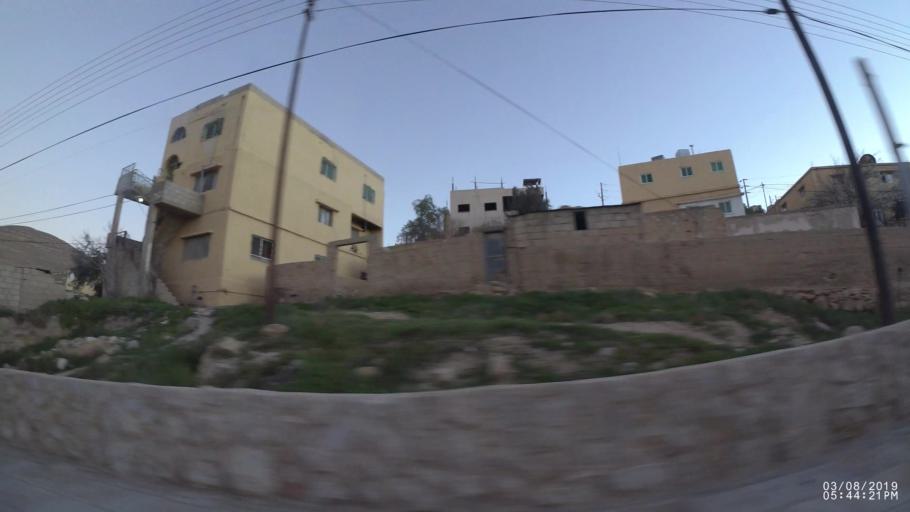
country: JO
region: Ma'an
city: Petra
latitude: 30.3117
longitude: 35.4816
